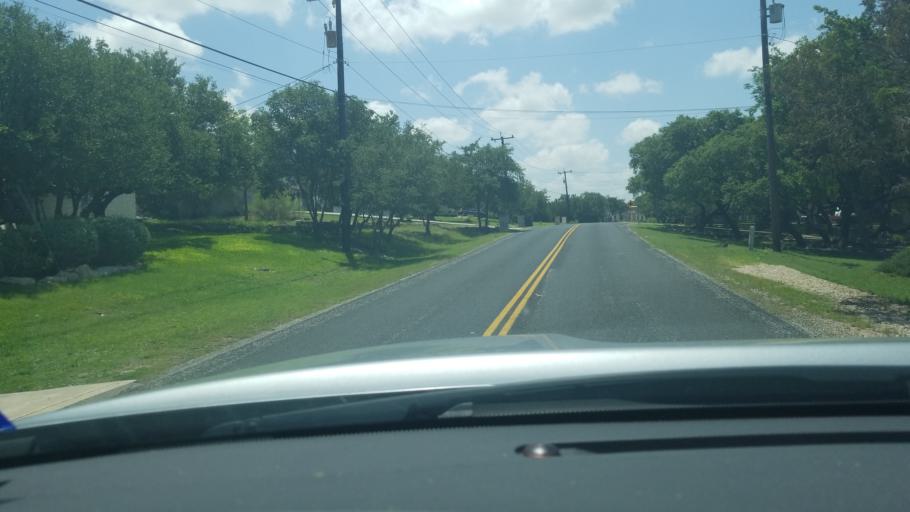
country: US
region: Texas
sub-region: Bexar County
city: Timberwood Park
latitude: 29.6874
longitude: -98.4871
